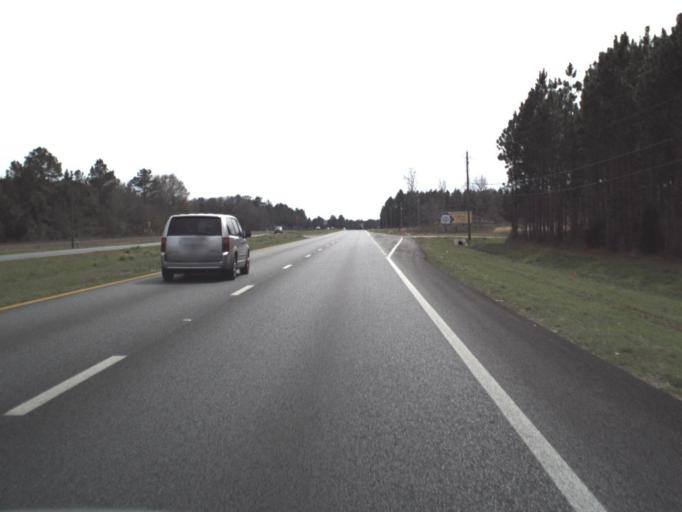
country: US
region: Florida
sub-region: Bay County
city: Youngstown
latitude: 30.3501
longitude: -85.4402
